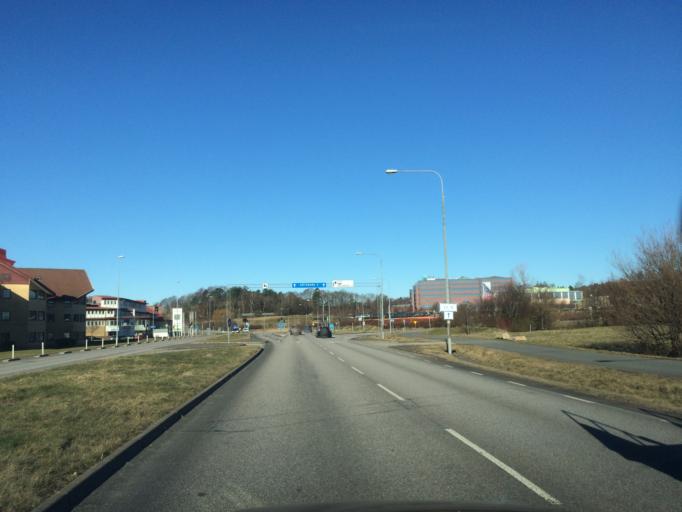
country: SE
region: Vaestra Goetaland
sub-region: Molndal
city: Moelndal
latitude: 57.6487
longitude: 11.9624
